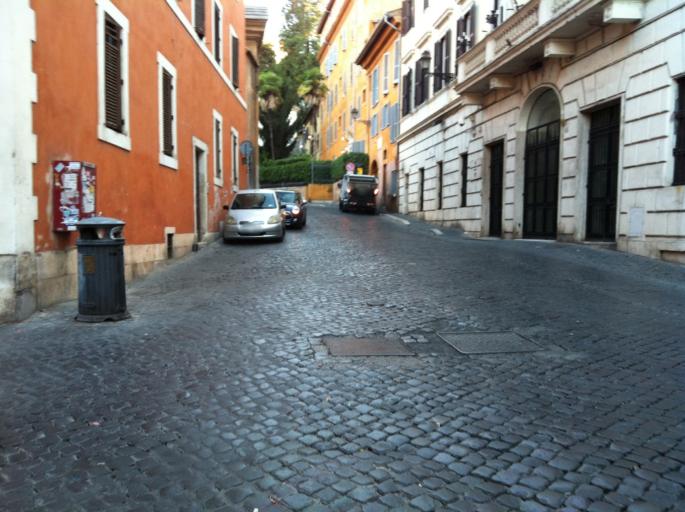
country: VA
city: Vatican City
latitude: 41.8904
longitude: 12.4662
